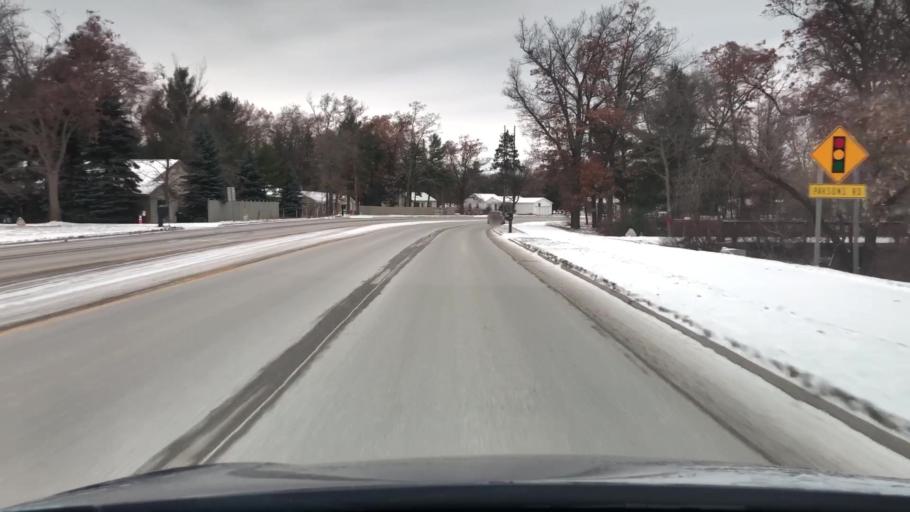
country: US
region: Michigan
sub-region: Grand Traverse County
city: Traverse City
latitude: 44.7438
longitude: -85.5608
